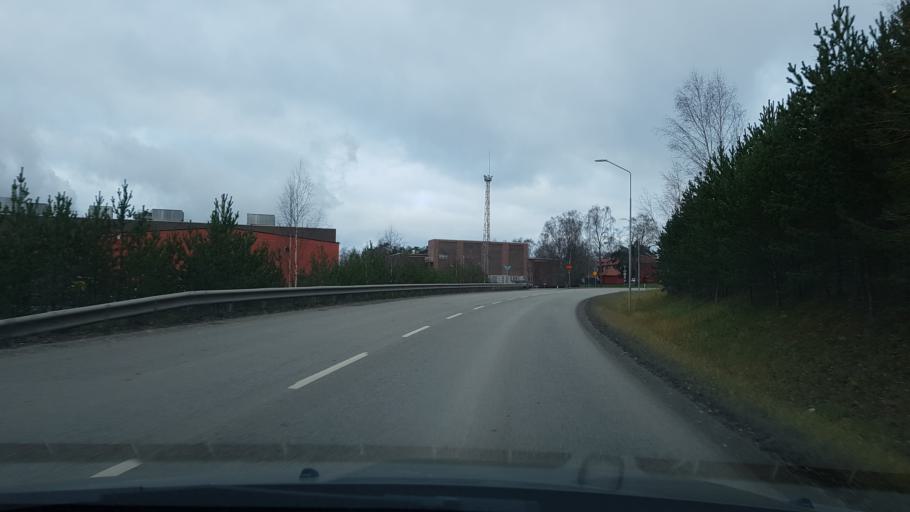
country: SE
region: Stockholm
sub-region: Norrtalje Kommun
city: Hallstavik
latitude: 60.0572
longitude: 18.5946
